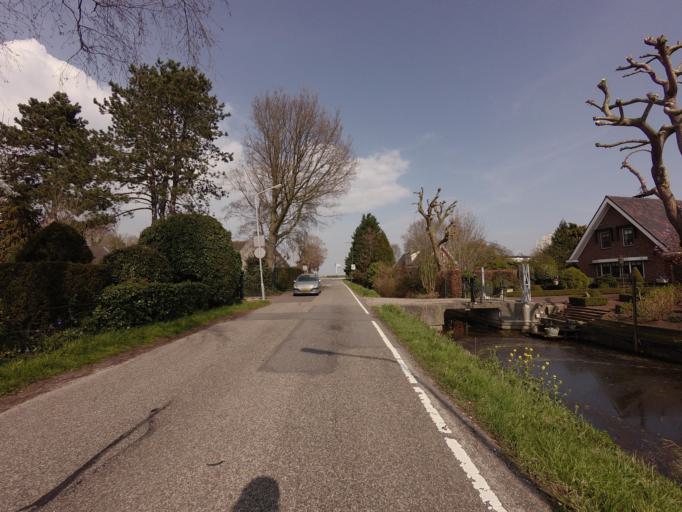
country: NL
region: North Holland
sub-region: Gemeente Wijdemeren
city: Kortenhoef
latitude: 52.2747
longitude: 5.1075
